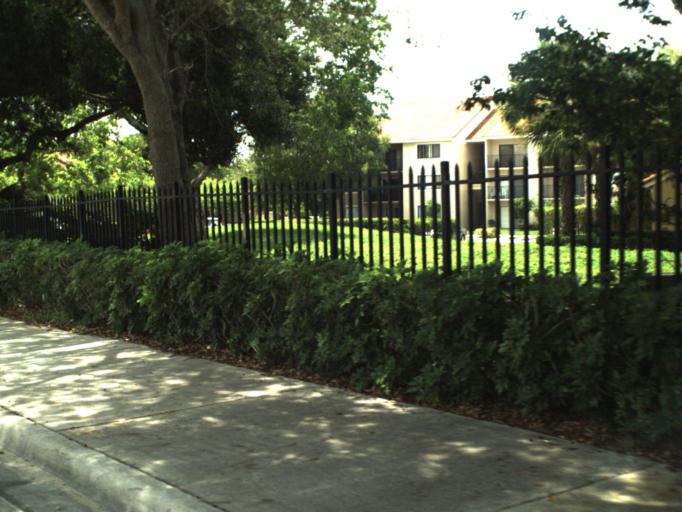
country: US
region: Florida
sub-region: Broward County
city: Tamarac
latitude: 26.2380
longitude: -80.2468
